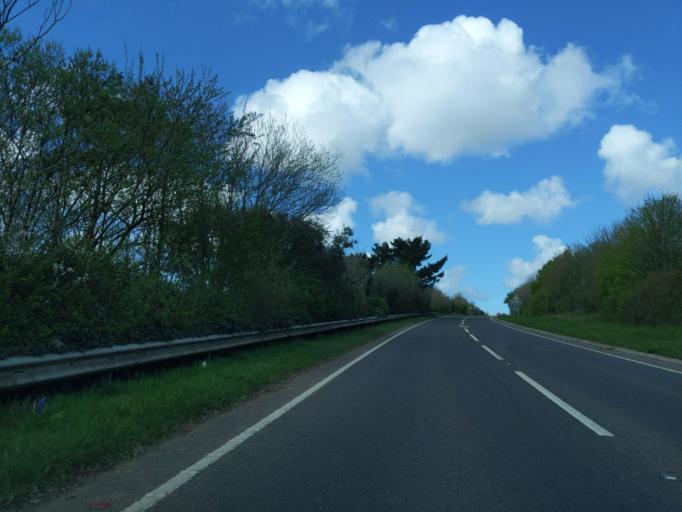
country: GB
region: England
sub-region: Cornwall
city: Wadebridge
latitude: 50.5142
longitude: -4.8183
